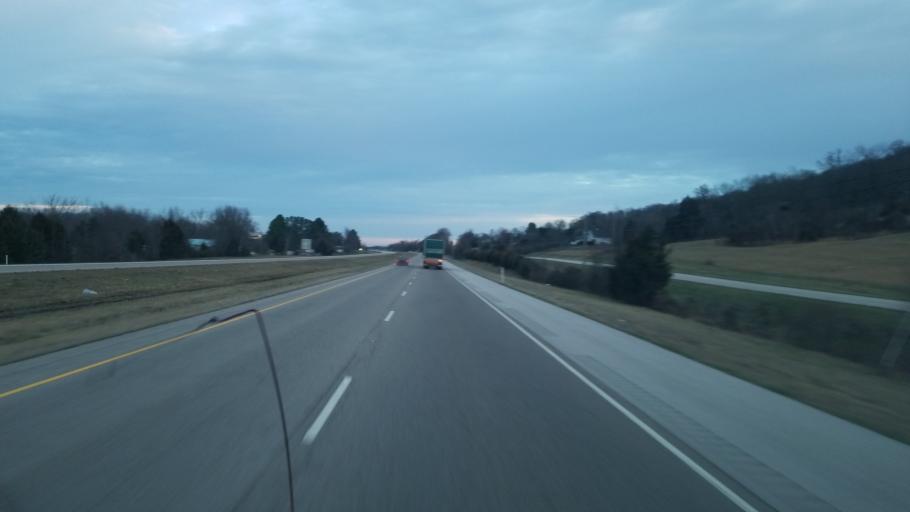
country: US
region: Tennessee
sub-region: White County
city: Sparta
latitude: 36.0023
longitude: -85.5035
